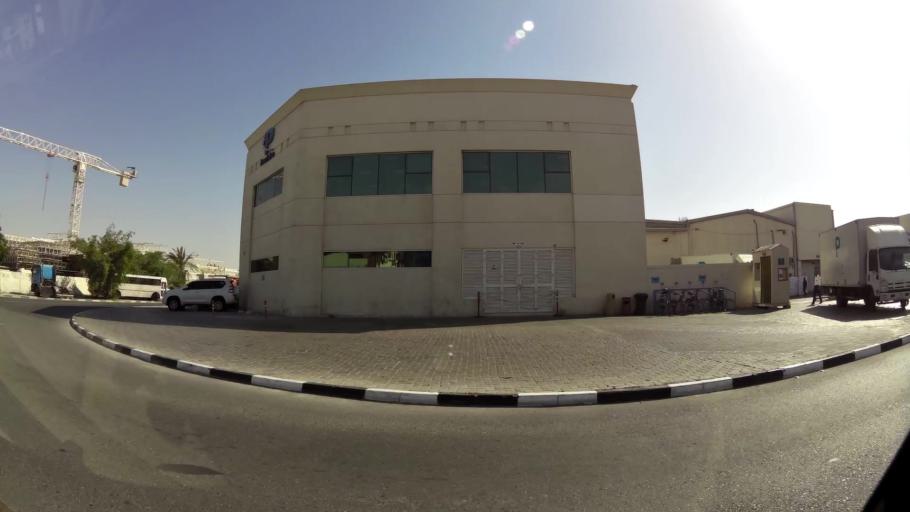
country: AE
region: Dubai
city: Dubai
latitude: 25.1310
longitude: 55.2254
